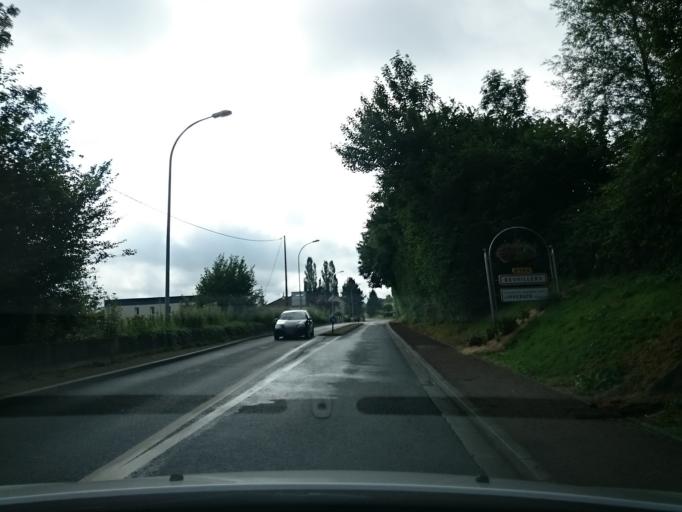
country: FR
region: Lower Normandy
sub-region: Departement du Calvados
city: Beuvillers
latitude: 49.1318
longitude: 0.2406
